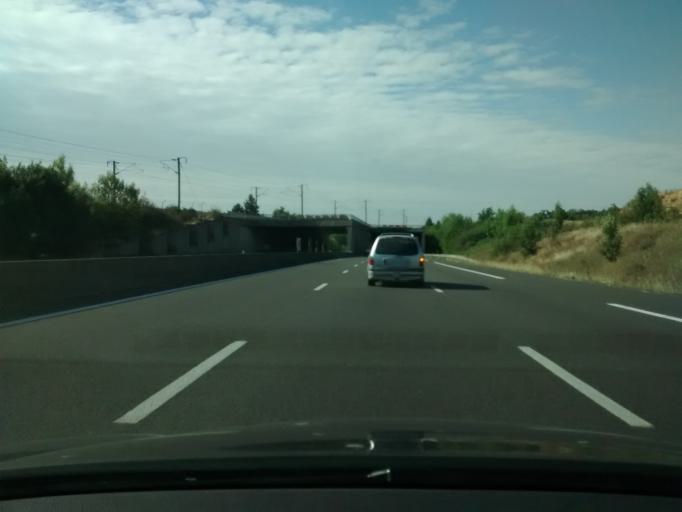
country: FR
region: Ile-de-France
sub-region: Departement de l'Essonne
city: Corbreuse
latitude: 48.5179
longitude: 1.9082
